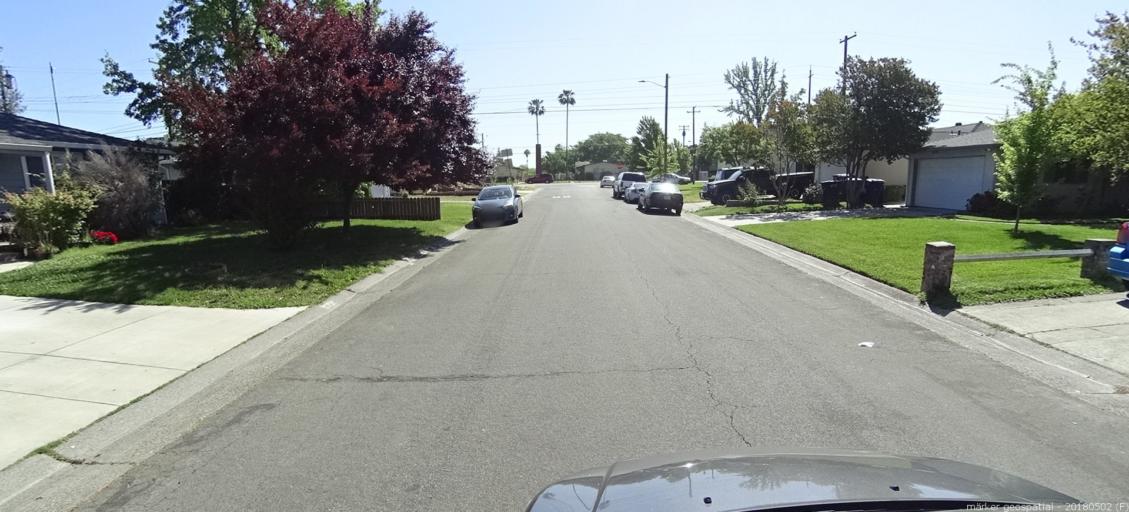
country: US
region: California
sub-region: Sacramento County
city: Arden-Arcade
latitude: 38.6020
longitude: -121.4211
